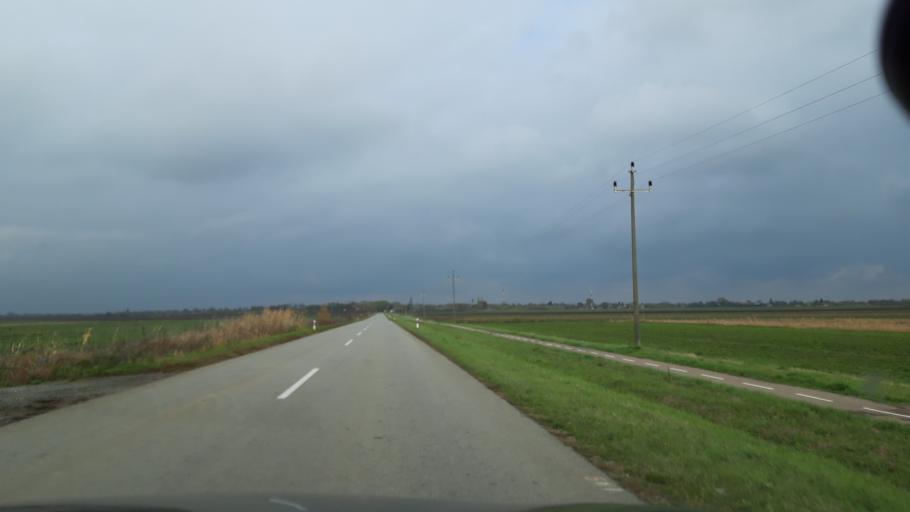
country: HU
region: Csongrad
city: Roszke
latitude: 46.1433
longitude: 20.0990
